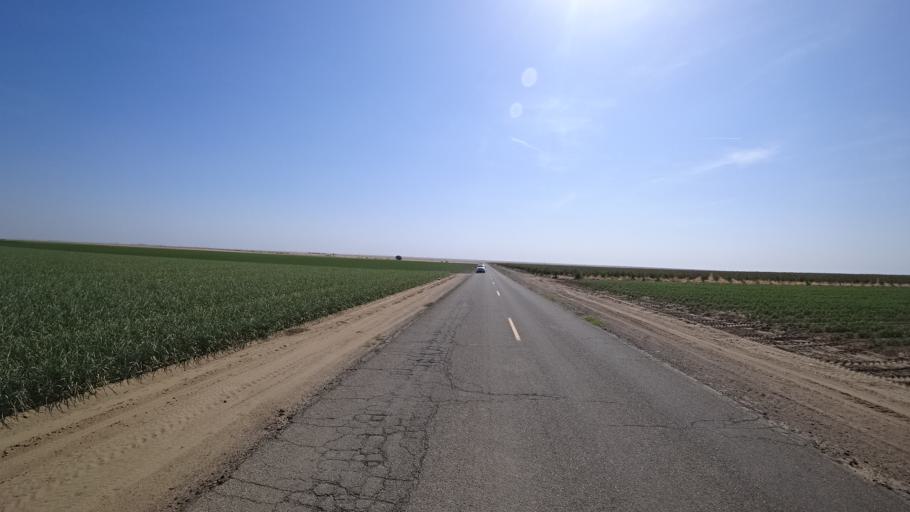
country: US
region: California
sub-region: Kings County
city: Kettleman City
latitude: 36.0363
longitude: -119.9775
